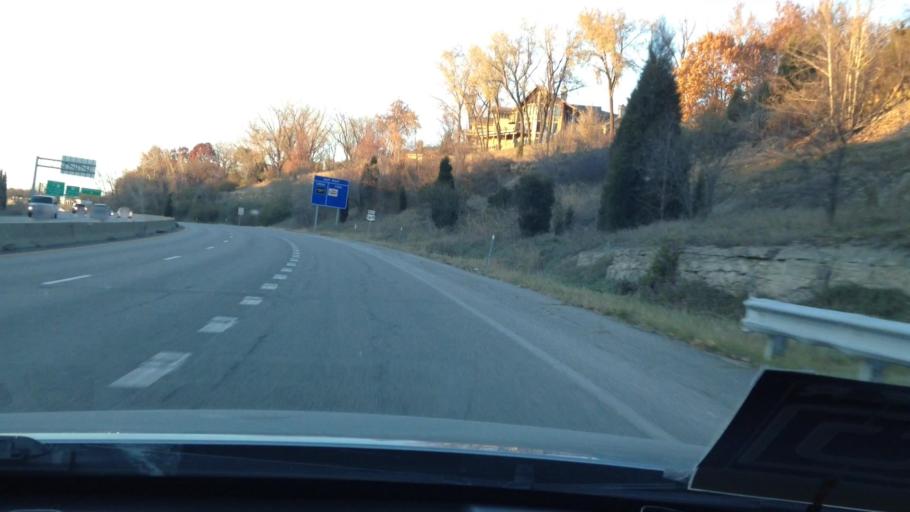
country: US
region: Missouri
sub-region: Platte County
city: Riverside
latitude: 39.1635
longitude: -94.5902
